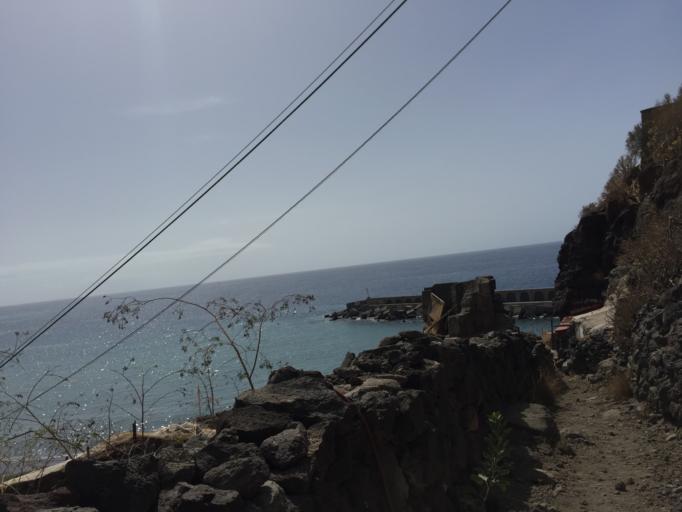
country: ES
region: Canary Islands
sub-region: Provincia de Santa Cruz de Tenerife
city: Tazacorte
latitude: 28.6523
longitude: -17.9478
